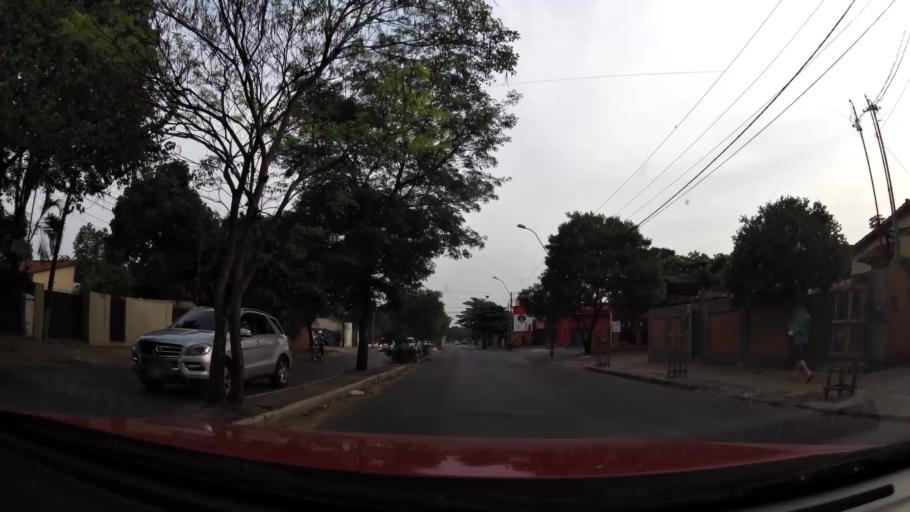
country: PY
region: Asuncion
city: Asuncion
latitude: -25.3064
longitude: -57.6150
